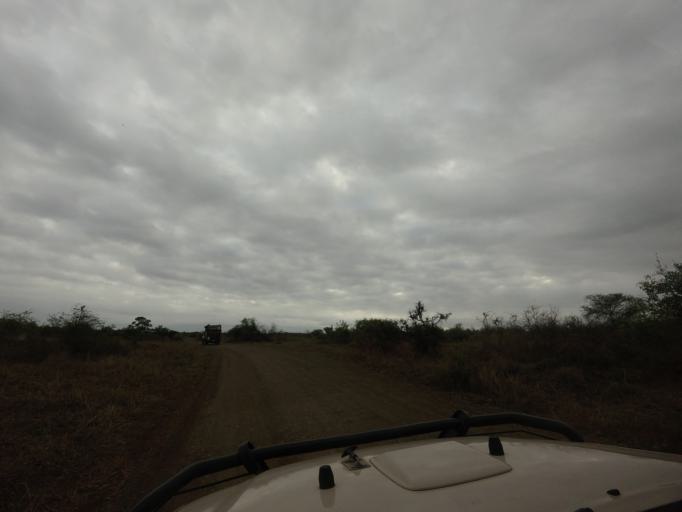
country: ZA
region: Mpumalanga
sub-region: Ehlanzeni District
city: Komatipoort
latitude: -25.3310
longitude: 31.9025
